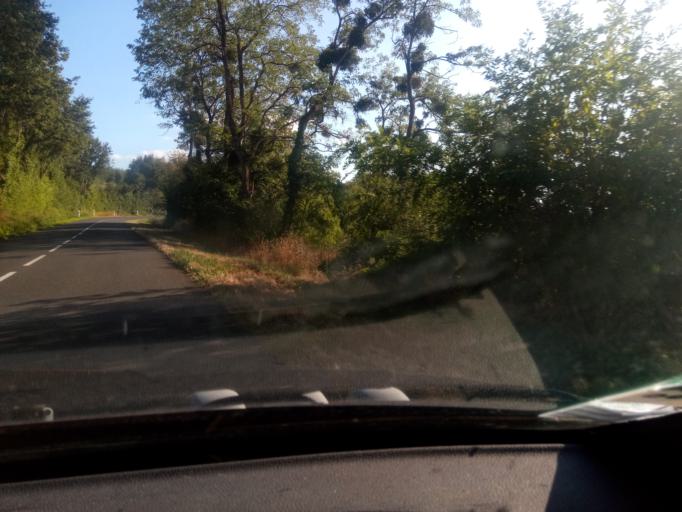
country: FR
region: Poitou-Charentes
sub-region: Departement de la Vienne
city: Availles-Limouzine
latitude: 46.2494
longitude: 0.6904
